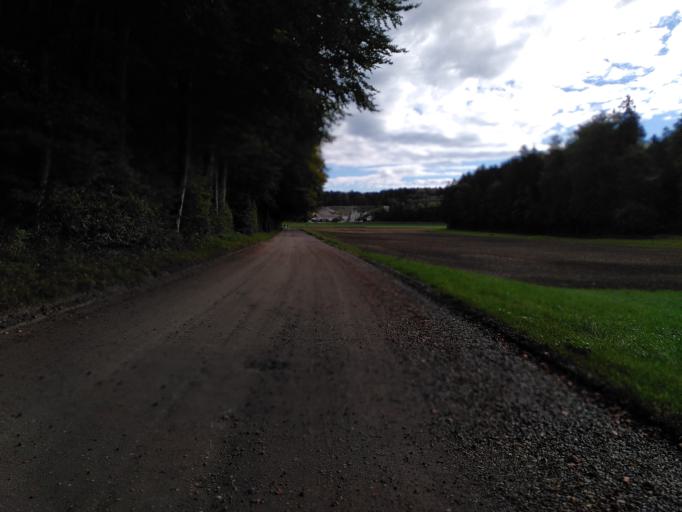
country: CH
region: Bern
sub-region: Emmental District
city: Wynigen
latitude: 47.0989
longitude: 7.6317
